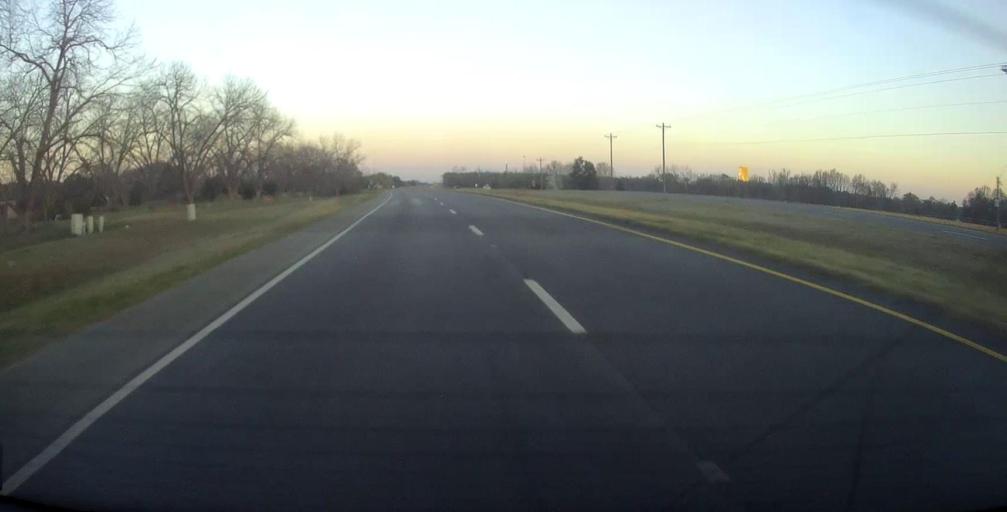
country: US
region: Georgia
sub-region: Dodge County
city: Eastman
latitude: 32.1540
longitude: -83.1448
